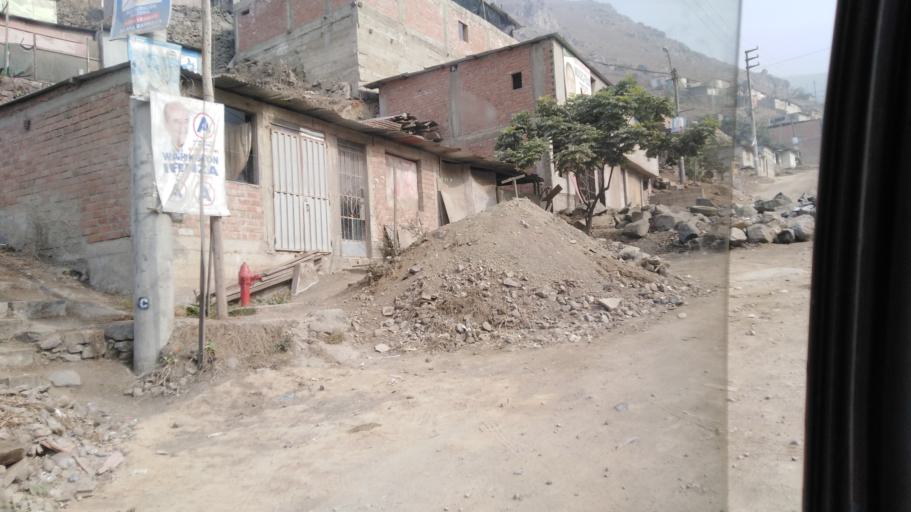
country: PE
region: Lima
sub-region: Lima
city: La Molina
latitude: -12.1426
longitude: -76.9249
